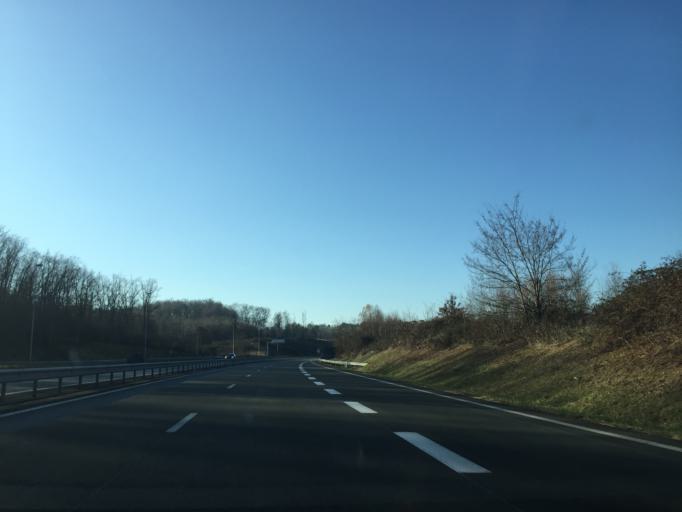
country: FR
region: Limousin
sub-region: Departement de la Correze
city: Saint-Pantaleon-de-Larche
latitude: 45.1617
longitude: 1.4364
